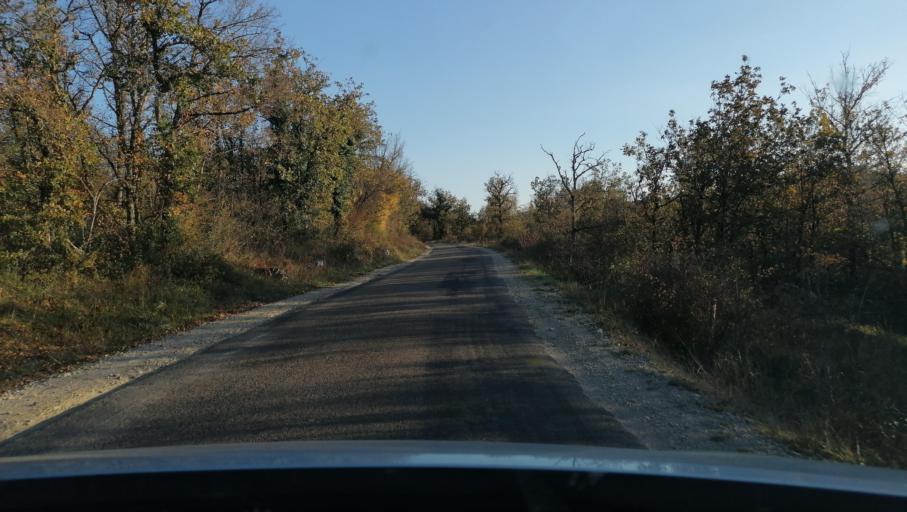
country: FR
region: Midi-Pyrenees
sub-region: Departement du Lot
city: Vayrac
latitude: 44.8697
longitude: 1.6653
